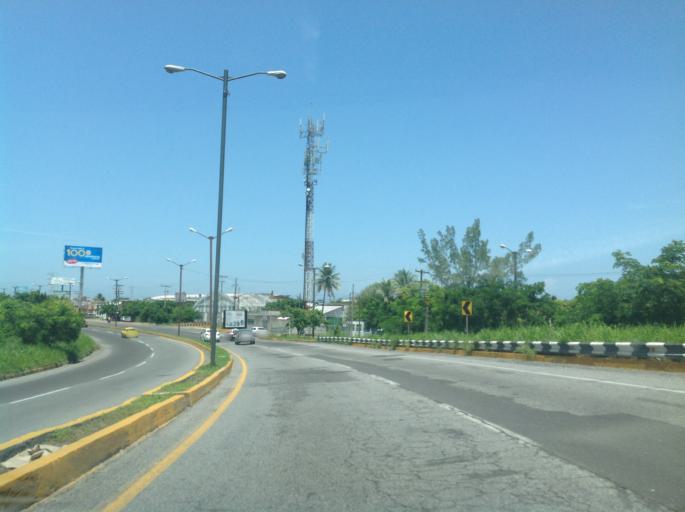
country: MX
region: Veracruz
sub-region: Veracruz
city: Hacienda Sotavento
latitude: 19.1415
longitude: -96.1468
